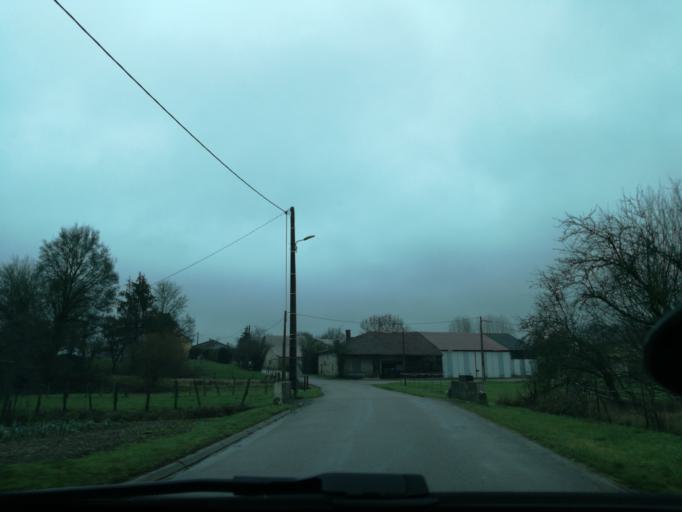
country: FR
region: Lorraine
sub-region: Departement de la Meuse
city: Clermont-en-Argonne
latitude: 49.0202
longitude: 5.1079
